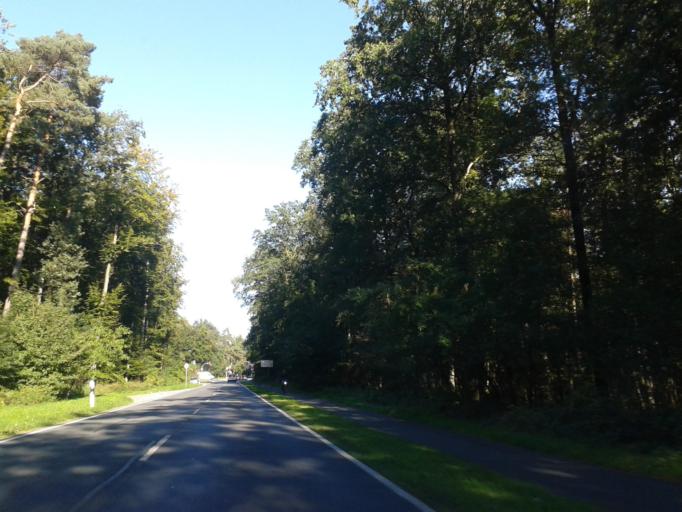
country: DE
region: North Rhine-Westphalia
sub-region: Regierungsbezirk Detmold
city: Paderborn
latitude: 51.7530
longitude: 8.7693
